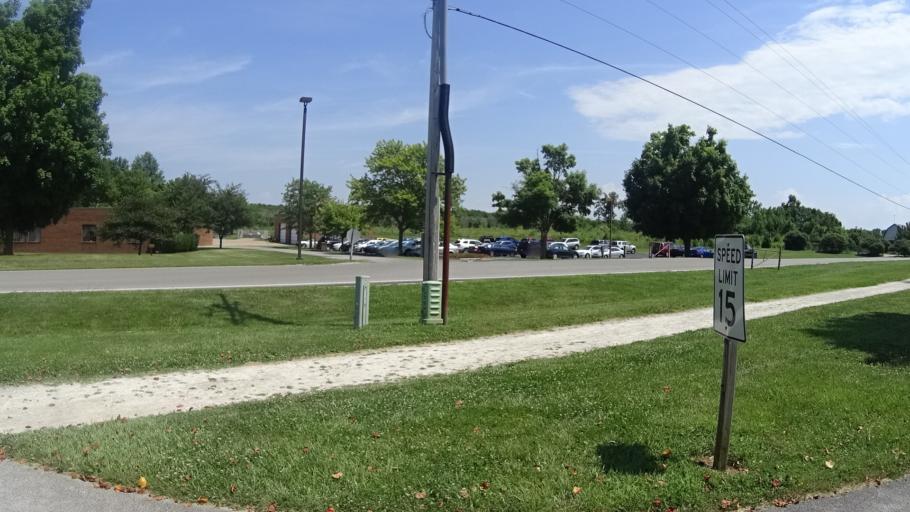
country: US
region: Ohio
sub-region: Erie County
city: Sandusky
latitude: 41.4171
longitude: -82.6361
